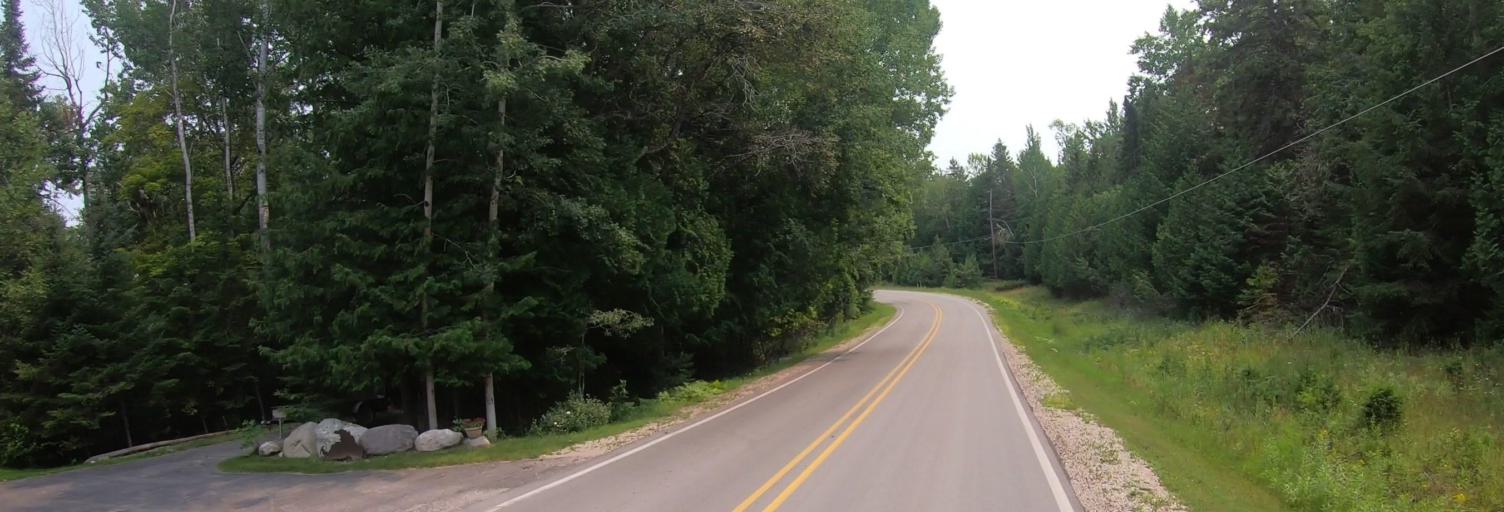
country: CA
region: Ontario
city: Thessalon
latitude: 46.0380
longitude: -83.7107
